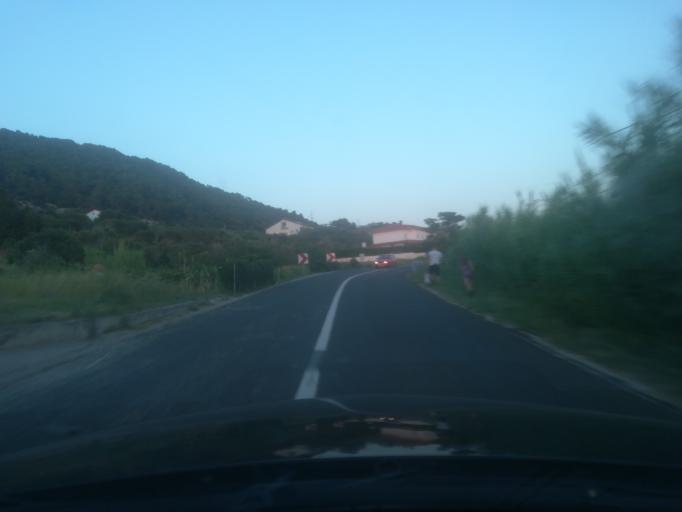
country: HR
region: Primorsko-Goranska
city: Banjol
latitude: 44.7421
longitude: 14.7979
